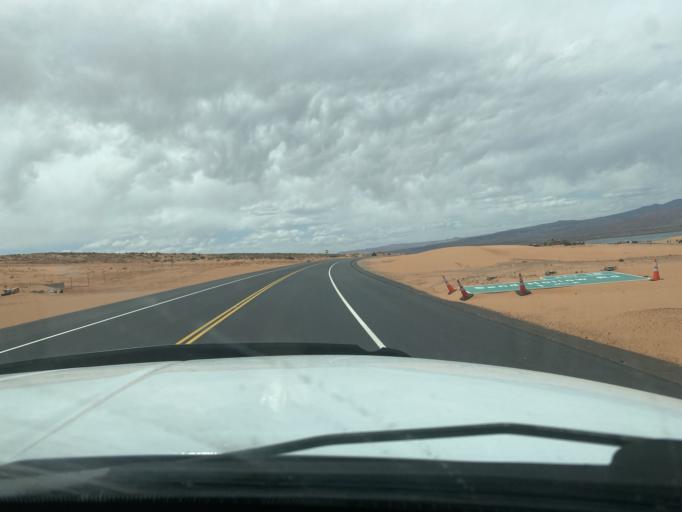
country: US
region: Utah
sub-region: Washington County
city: Hurricane
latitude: 37.0992
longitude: -113.3763
